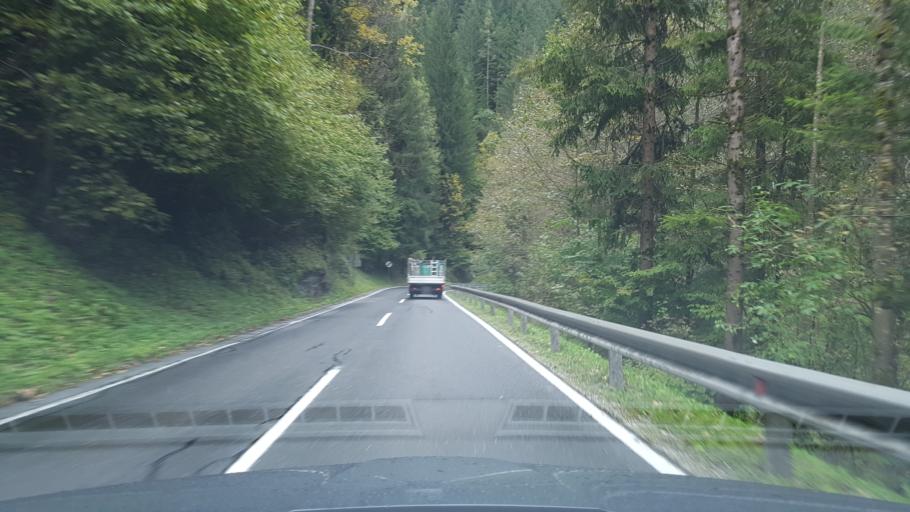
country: AT
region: Styria
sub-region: Politischer Bezirk Voitsberg
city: Salla
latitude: 47.1093
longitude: 15.0120
